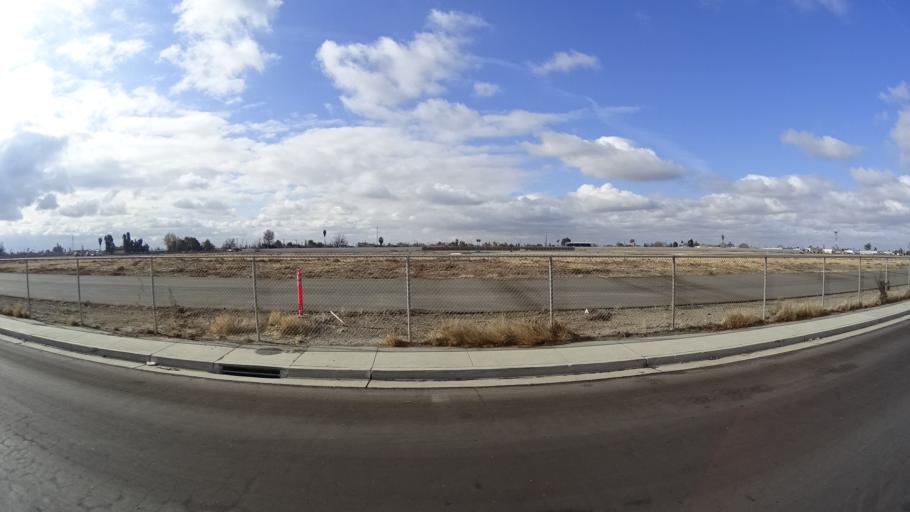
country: US
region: California
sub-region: Kern County
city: Greenfield
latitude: 35.3198
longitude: -118.9940
